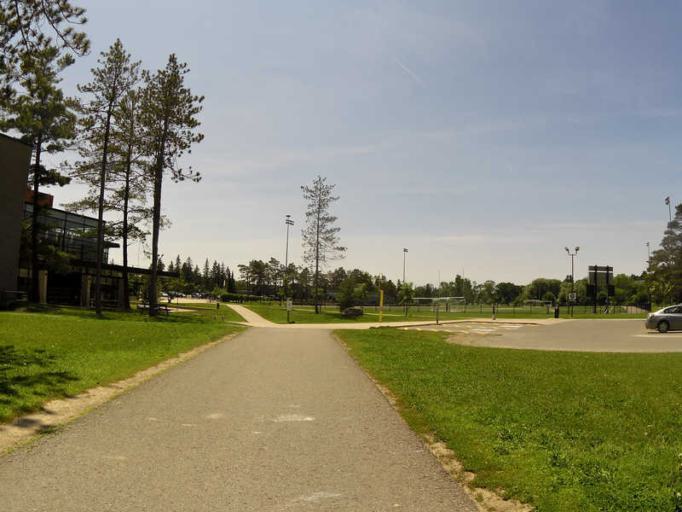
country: CA
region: Ontario
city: Peterborough
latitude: 44.3557
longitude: -78.2928
